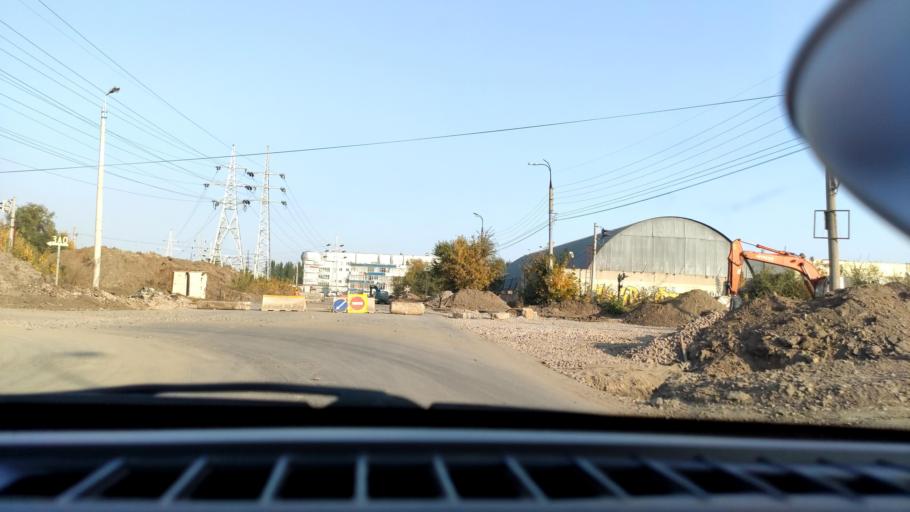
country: RU
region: Samara
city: Samara
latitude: 53.1941
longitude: 50.2404
